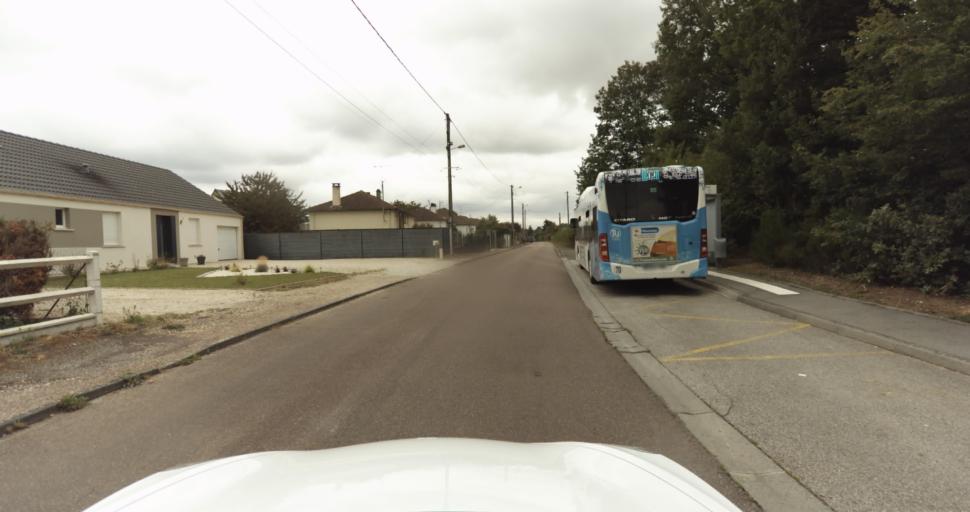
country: FR
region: Haute-Normandie
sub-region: Departement de l'Eure
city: Saint-Sebastien-de-Morsent
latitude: 49.0163
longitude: 1.0954
